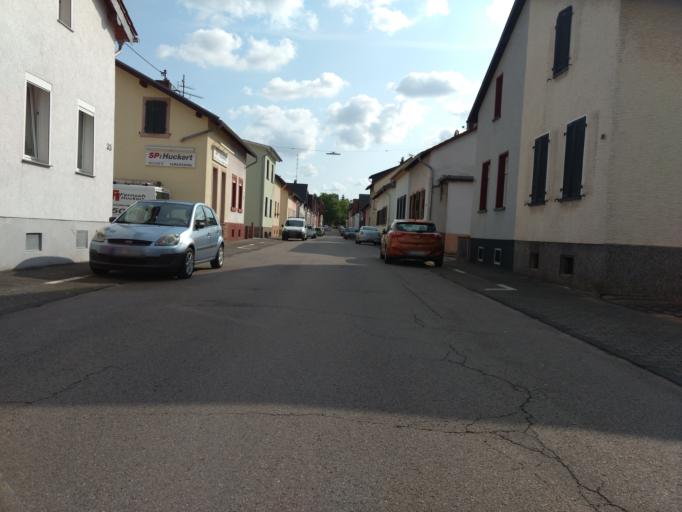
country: DE
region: Saarland
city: Merzig
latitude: 49.4410
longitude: 6.6408
